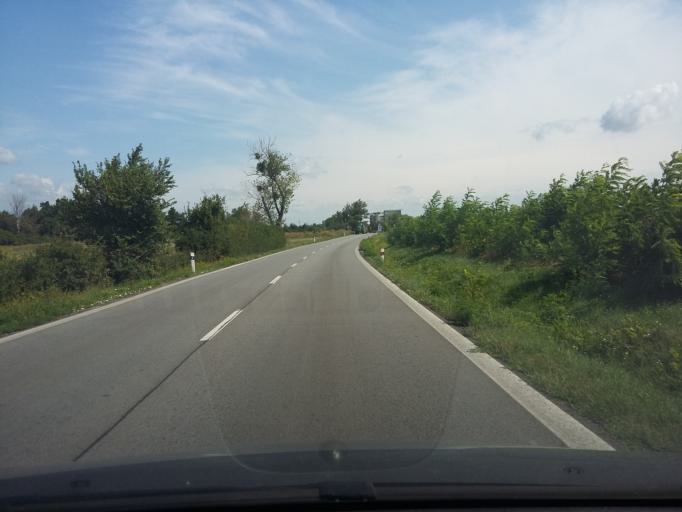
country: SK
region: Bratislavsky
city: Svaty Jur
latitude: 48.2398
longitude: 17.2549
